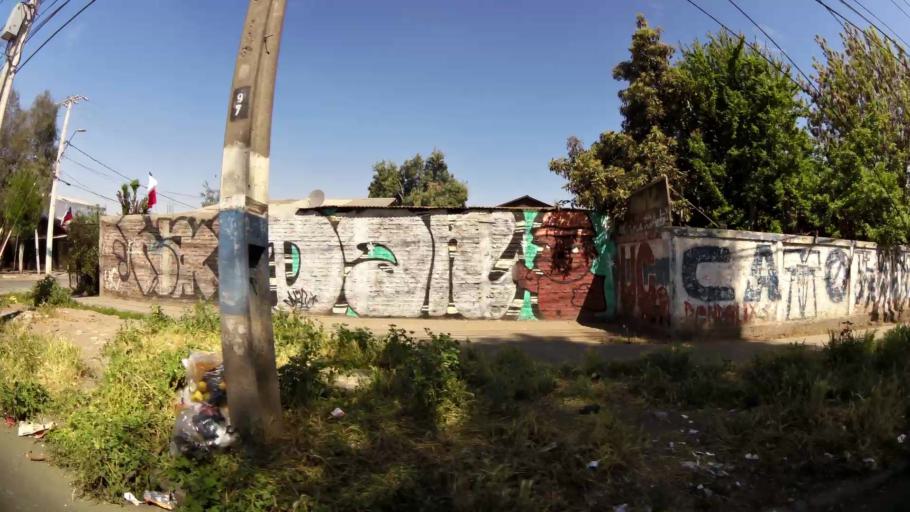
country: CL
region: Santiago Metropolitan
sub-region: Provincia de Santiago
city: Lo Prado
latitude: -33.4065
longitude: -70.7360
